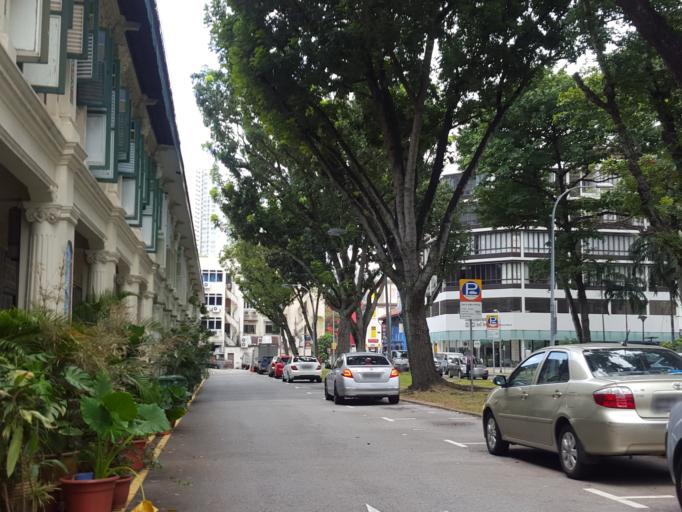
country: SG
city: Singapore
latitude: 1.3123
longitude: 103.8582
